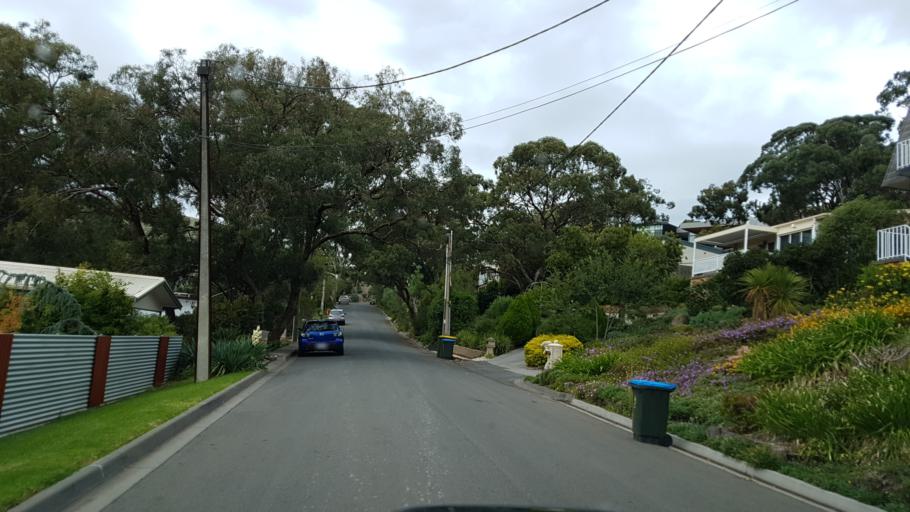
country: AU
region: South Australia
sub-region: Mitcham
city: Mitcham
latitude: -34.9850
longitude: 138.6231
